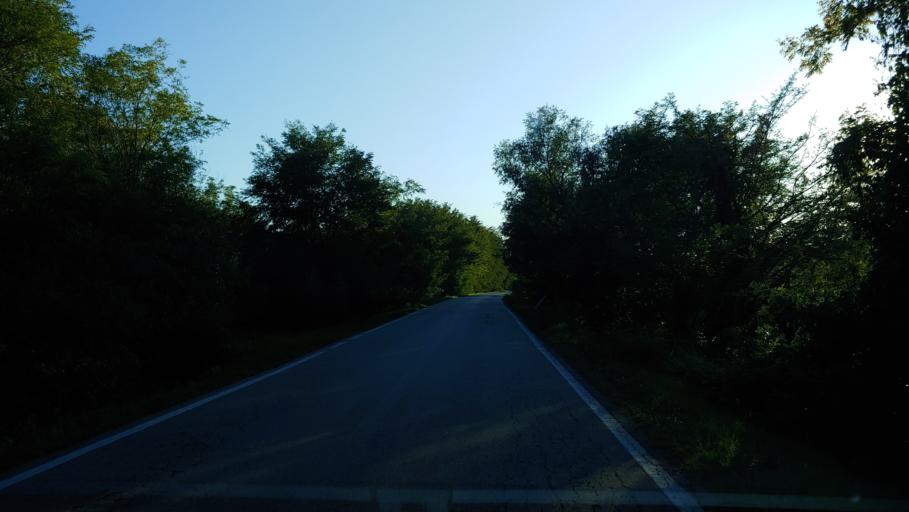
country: IT
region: Veneto
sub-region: Provincia di Rovigo
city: Villanova Marchesana
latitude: 45.0428
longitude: 11.9761
